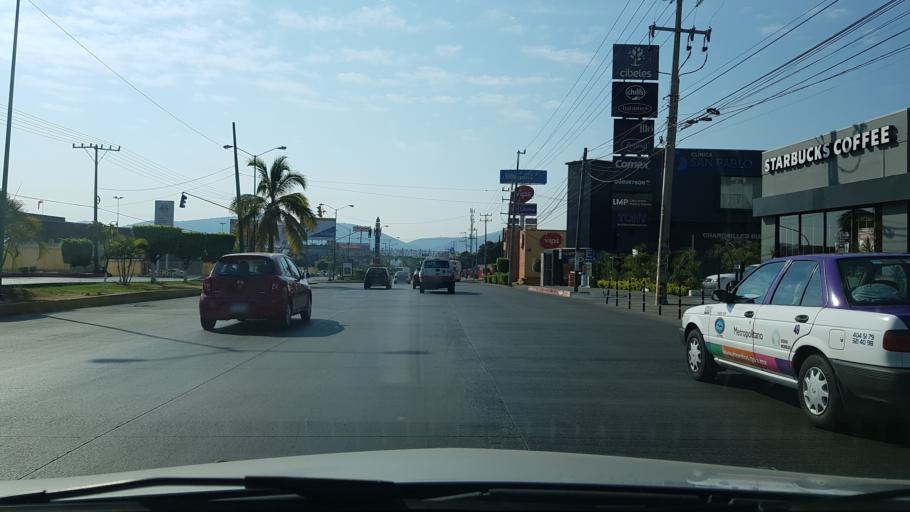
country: MX
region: Morelos
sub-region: Jiutepec
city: Jiutepec
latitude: 18.9039
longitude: -99.1758
